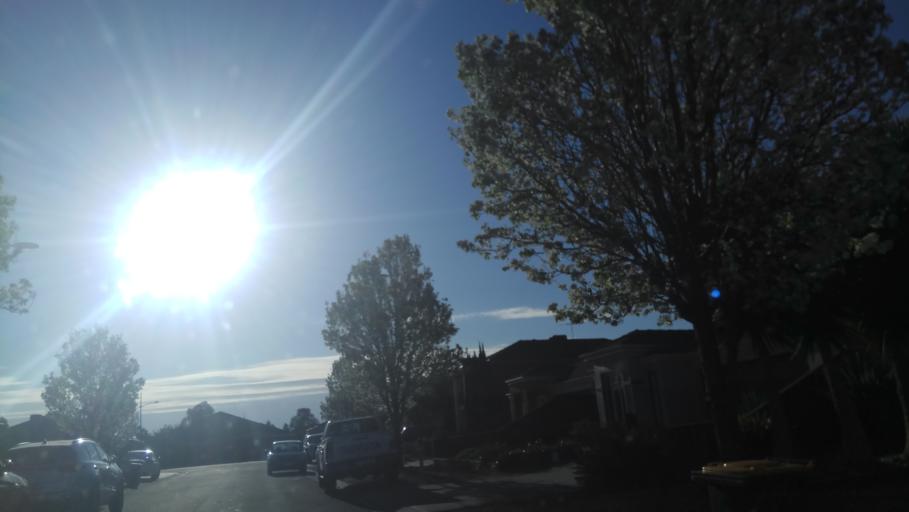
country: AU
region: Victoria
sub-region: Wyndham
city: Point Cook
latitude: -37.9061
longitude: 144.7462
